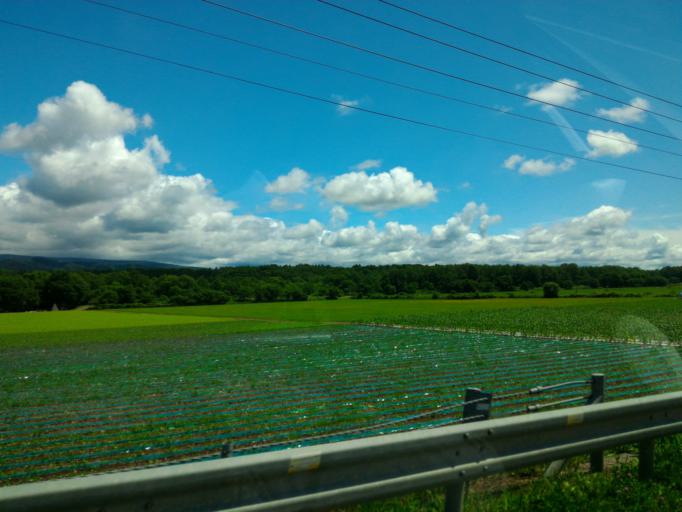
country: JP
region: Hokkaido
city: Nayoro
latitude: 44.5234
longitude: 142.3265
